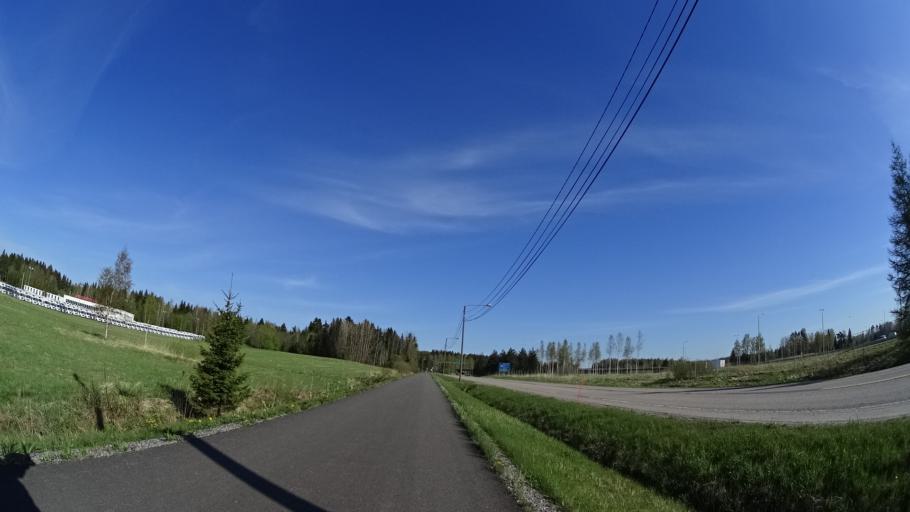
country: FI
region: Uusimaa
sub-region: Helsinki
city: Nurmijaervi
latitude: 60.3513
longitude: 24.8080
